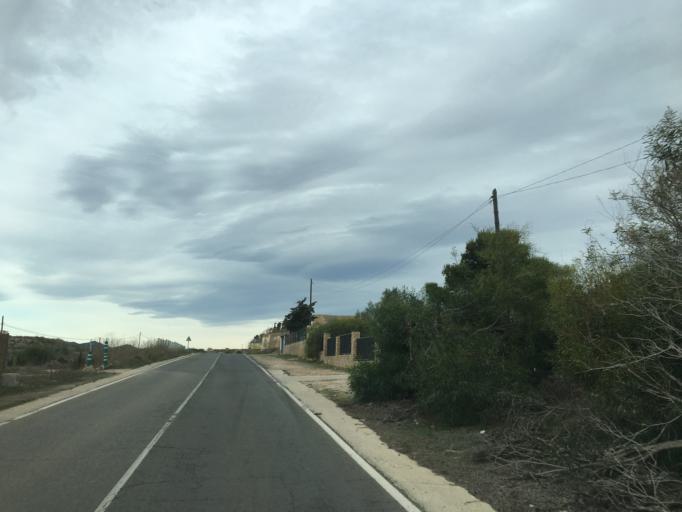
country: ES
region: Murcia
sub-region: Murcia
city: Cartagena
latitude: 37.6133
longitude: -1.0590
